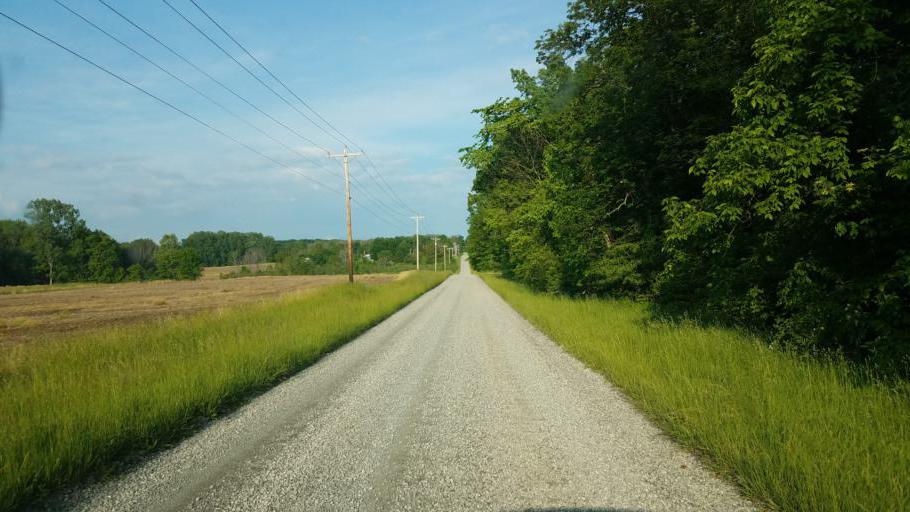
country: US
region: Ohio
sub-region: Morrow County
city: Cardington
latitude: 40.4240
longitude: -82.7939
